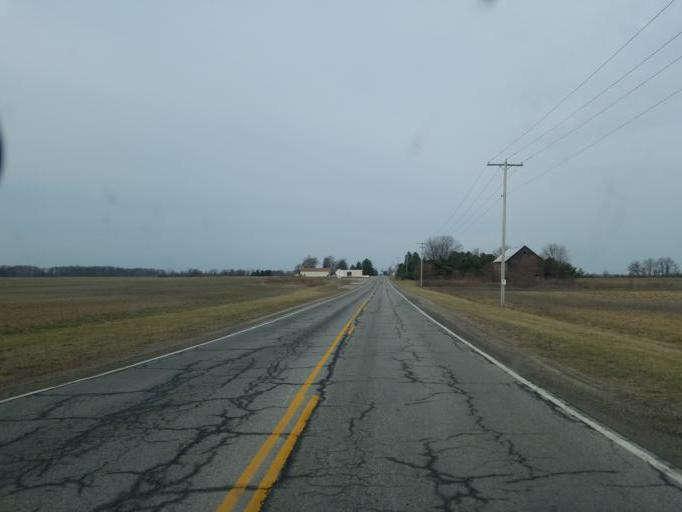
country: US
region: Ohio
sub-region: Marion County
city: Marion
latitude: 40.6303
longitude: -83.0262
